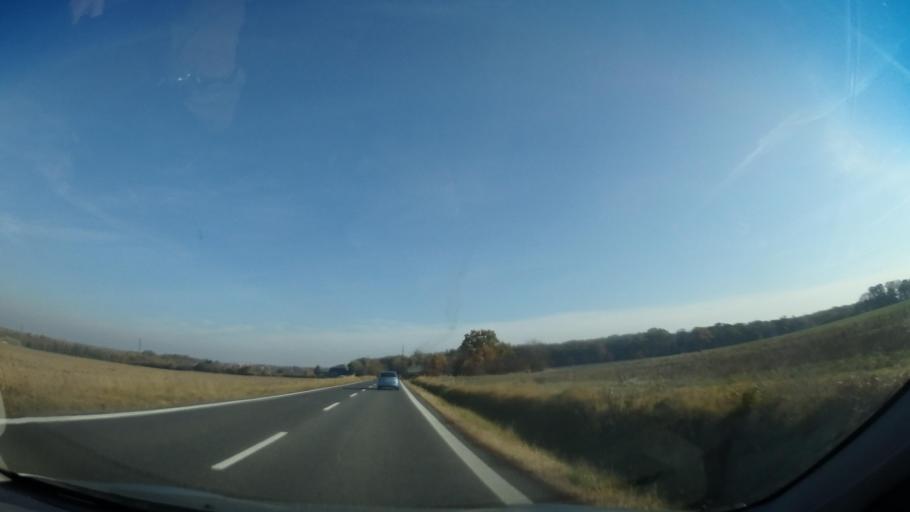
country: CZ
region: Praha
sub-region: Praha 20
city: Horni Pocernice
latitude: 50.0629
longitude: 14.6227
